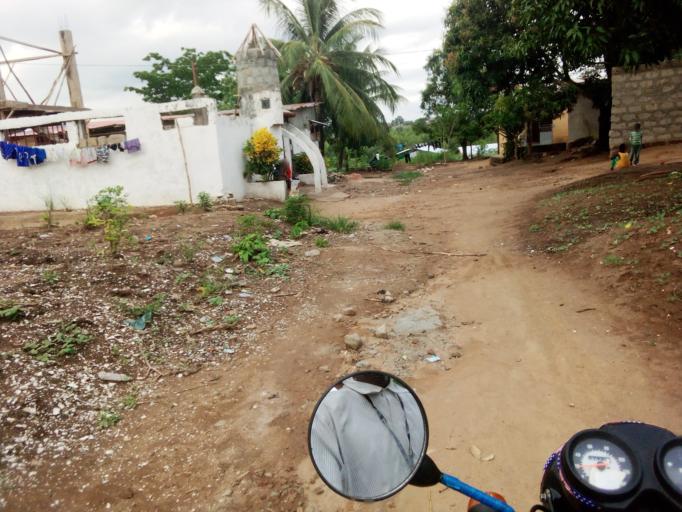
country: SL
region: Western Area
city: Waterloo
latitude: 8.3445
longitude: -13.0688
